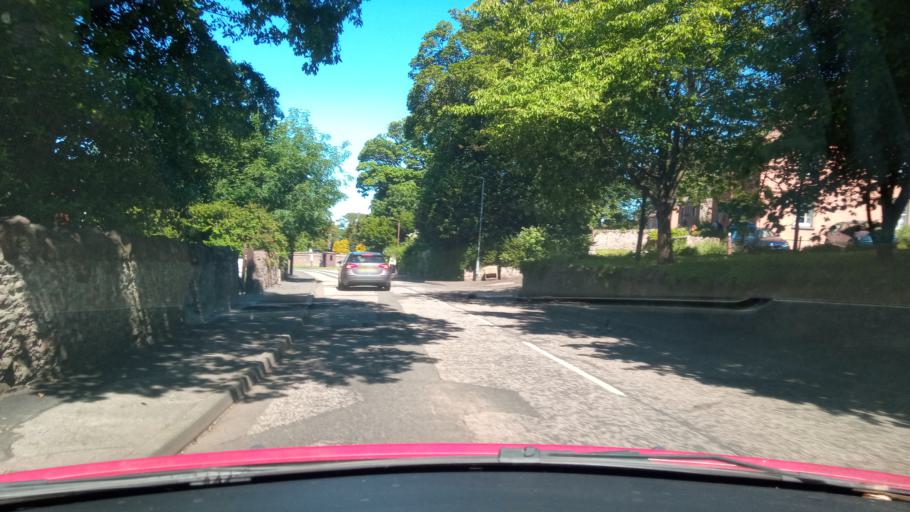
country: GB
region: Scotland
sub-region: East Lothian
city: Gullane
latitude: 56.0450
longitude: -2.7823
